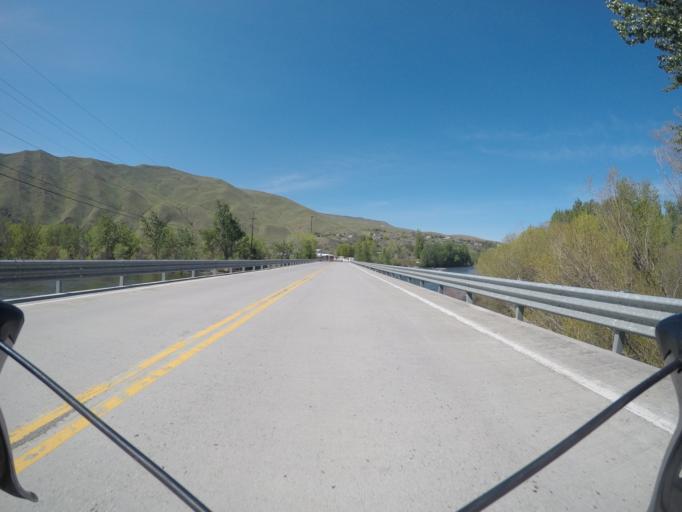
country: US
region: Washington
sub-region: Chelan County
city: West Wenatchee
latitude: 47.4725
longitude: -120.3709
